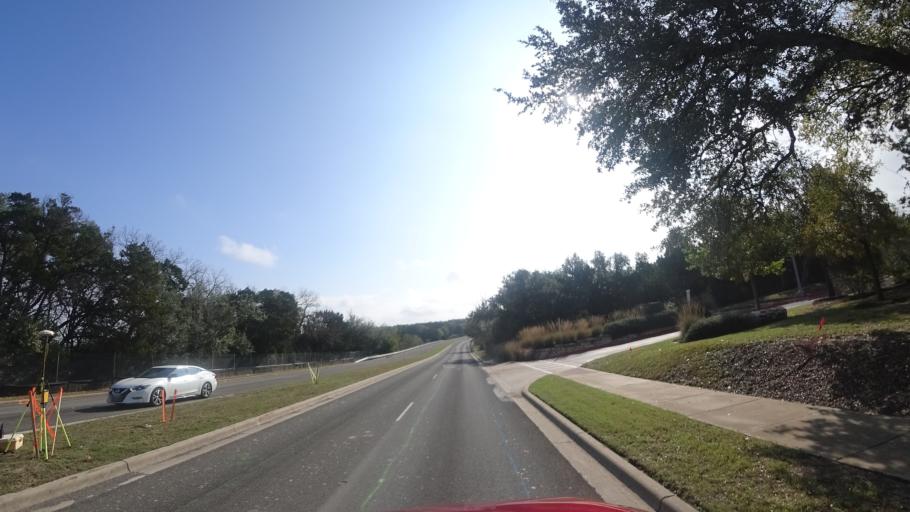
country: US
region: Texas
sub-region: Williamson County
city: Anderson Mill
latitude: 30.4047
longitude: -97.8484
